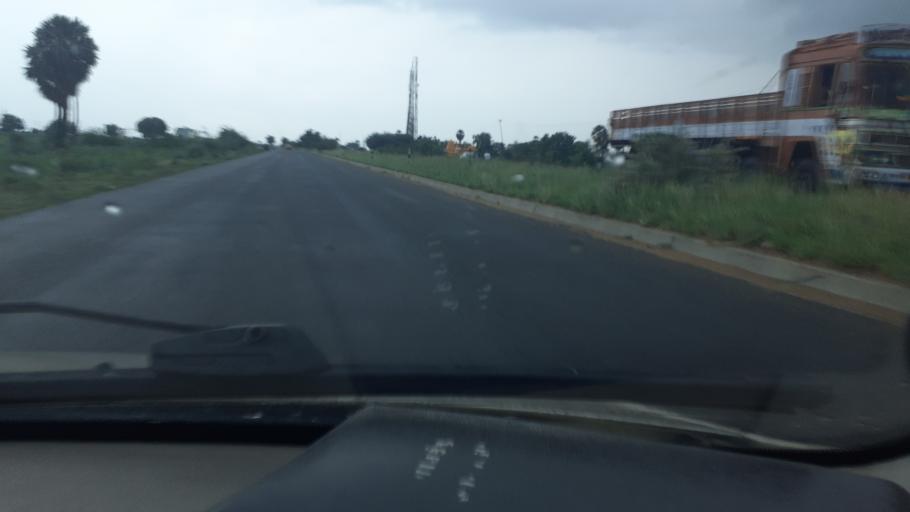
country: IN
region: Tamil Nadu
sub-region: Thoothukkudi
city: Kadambur
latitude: 9.0678
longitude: 77.7989
